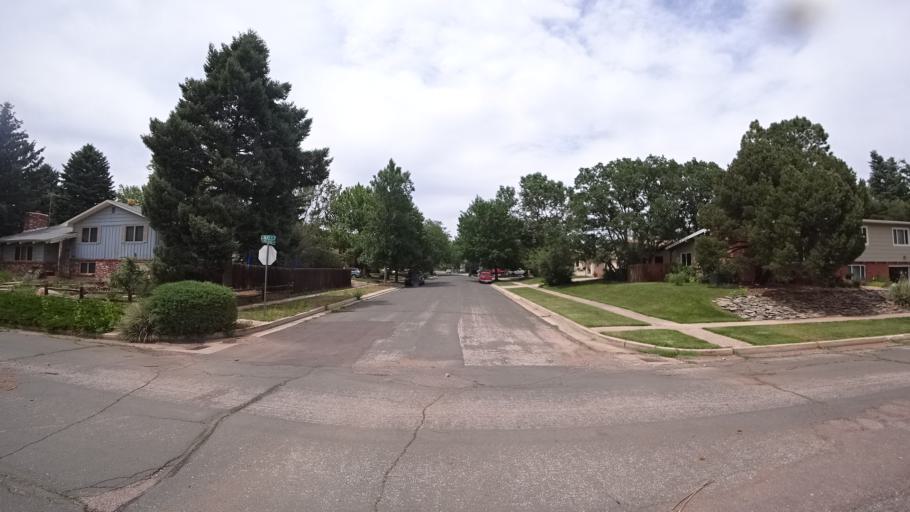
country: US
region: Colorado
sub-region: El Paso County
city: Manitou Springs
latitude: 38.8690
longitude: -104.8697
